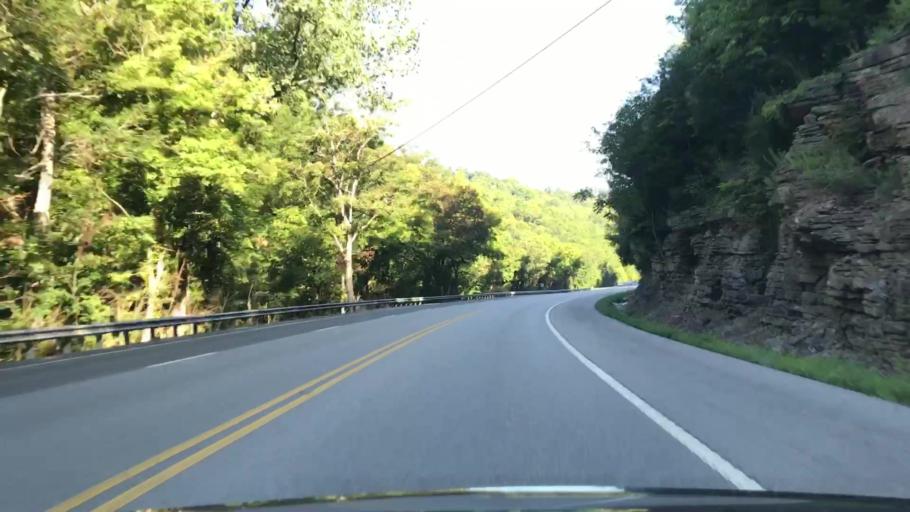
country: US
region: Tennessee
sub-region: Jackson County
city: Gainesboro
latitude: 36.3151
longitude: -85.6507
